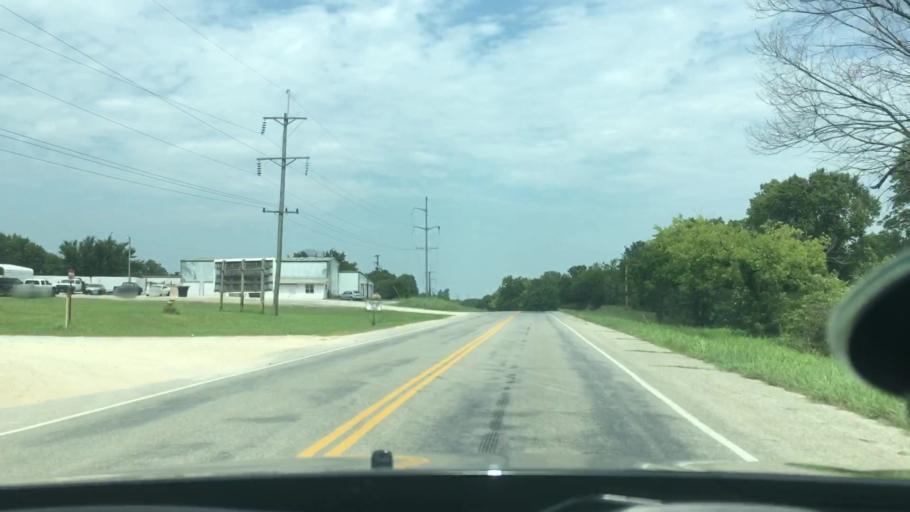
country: US
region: Oklahoma
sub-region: Pontotoc County
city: Byng
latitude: 34.8293
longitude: -96.6786
